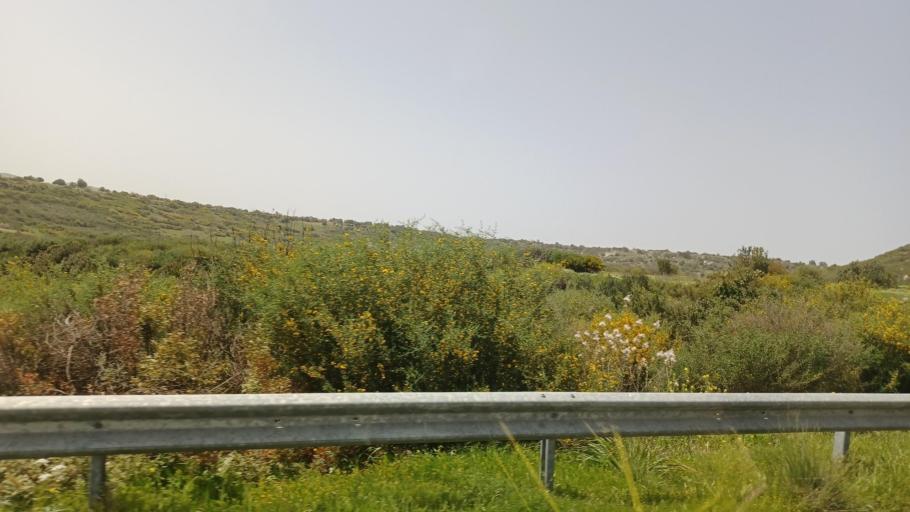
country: CY
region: Limassol
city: Pissouri
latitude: 34.7211
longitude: 32.7373
